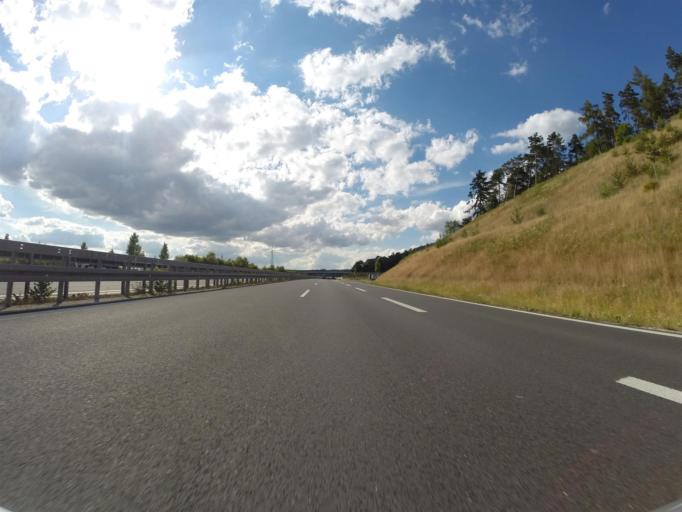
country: DE
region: Bavaria
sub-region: Upper Franconia
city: Rodental
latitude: 50.2499
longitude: 11.0337
